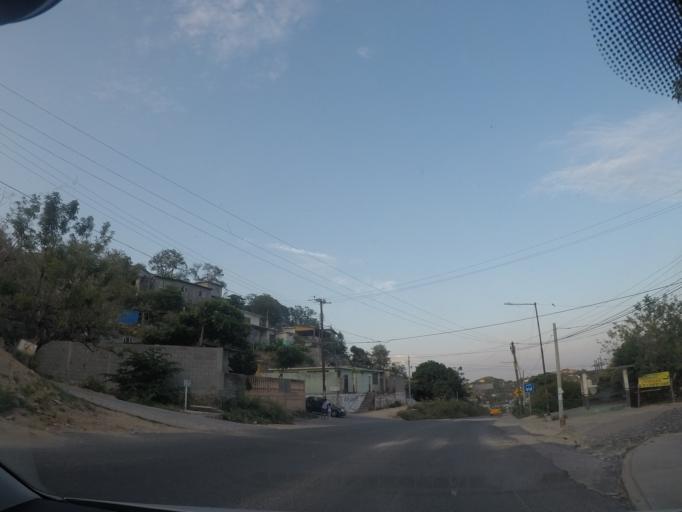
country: MX
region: Oaxaca
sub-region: Salina Cruz
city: Salina Cruz
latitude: 16.1928
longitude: -95.2096
